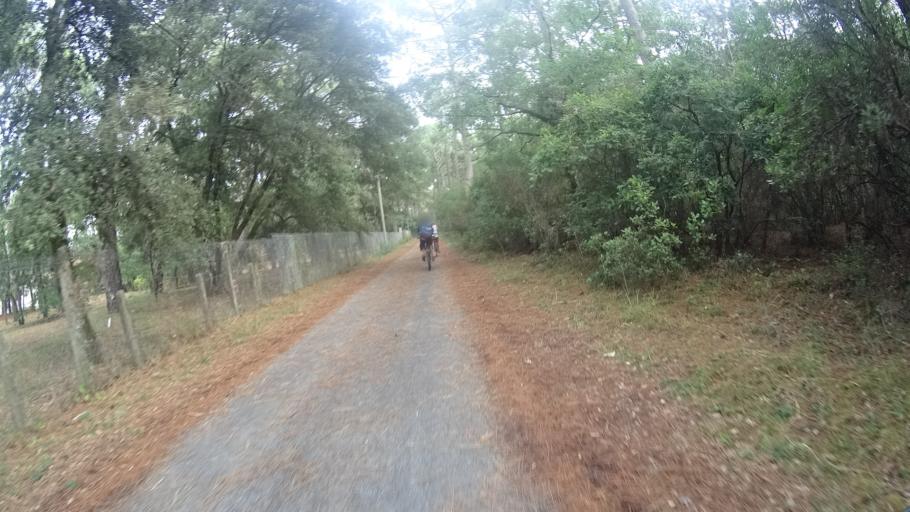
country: FR
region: Aquitaine
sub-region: Departement de la Gironde
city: Lacanau
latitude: 44.9898
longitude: -1.1400
